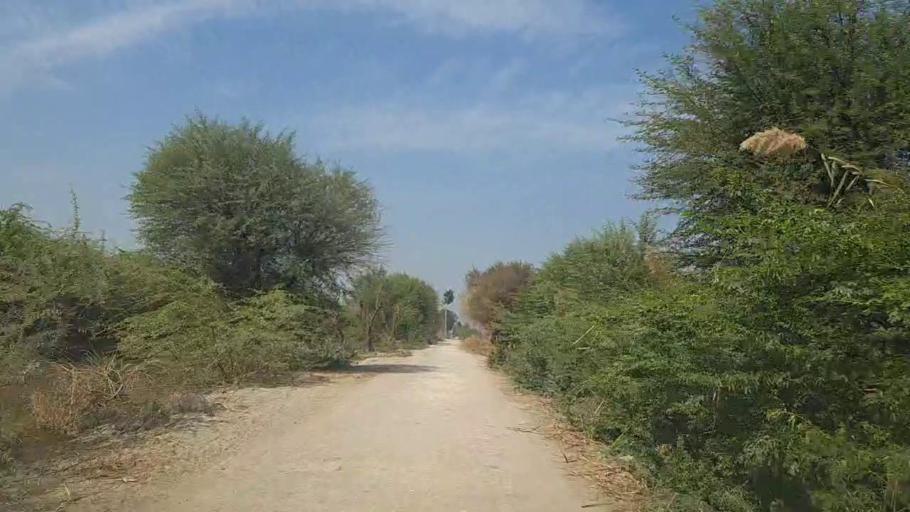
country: PK
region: Sindh
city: Mirpur Khas
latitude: 25.4853
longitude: 68.9265
